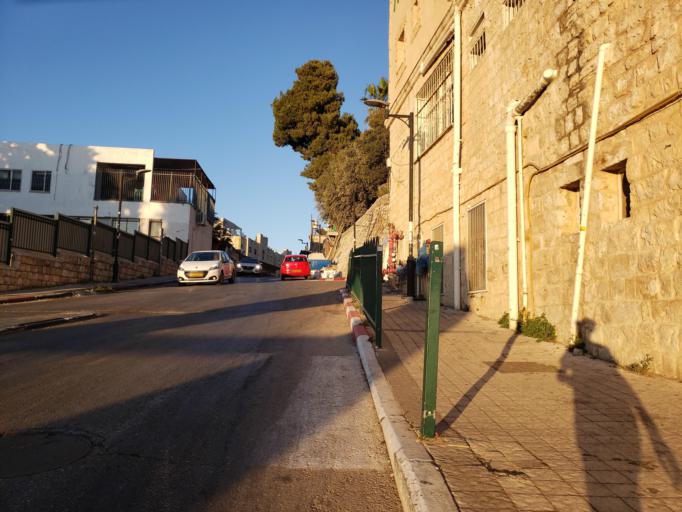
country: IL
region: Northern District
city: Safed
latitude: 32.9718
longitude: 35.4928
